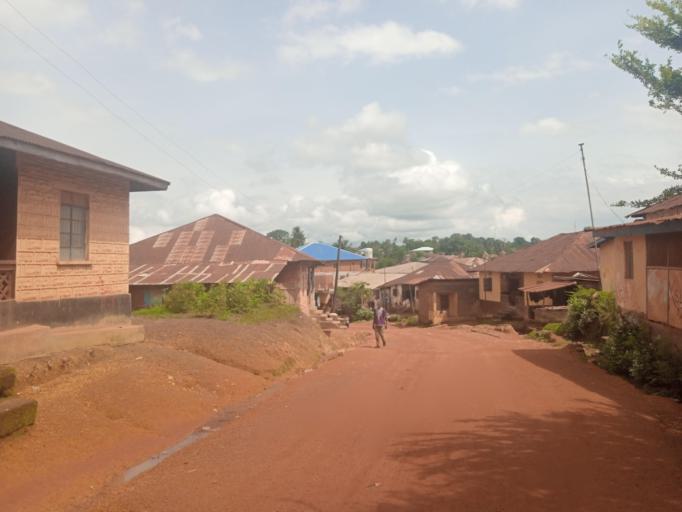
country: SL
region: Southern Province
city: Bo
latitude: 7.9684
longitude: -11.7361
